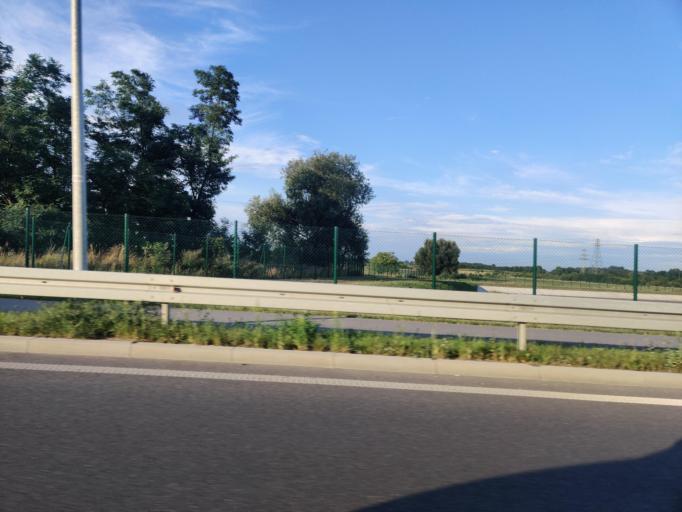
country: PL
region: Greater Poland Voivodeship
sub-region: Konin
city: Konin
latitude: 52.2049
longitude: 18.2693
